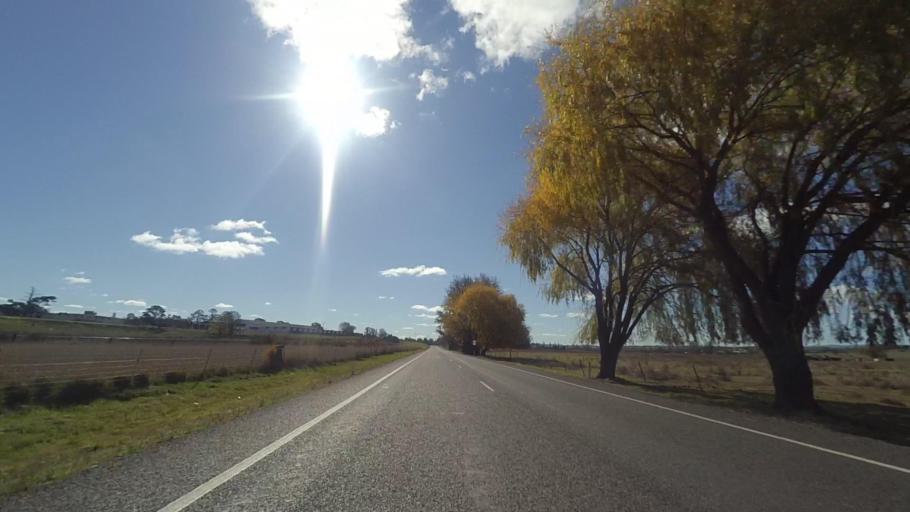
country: AU
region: New South Wales
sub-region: Bathurst Regional
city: Bathurst
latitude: -33.4468
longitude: 149.5789
